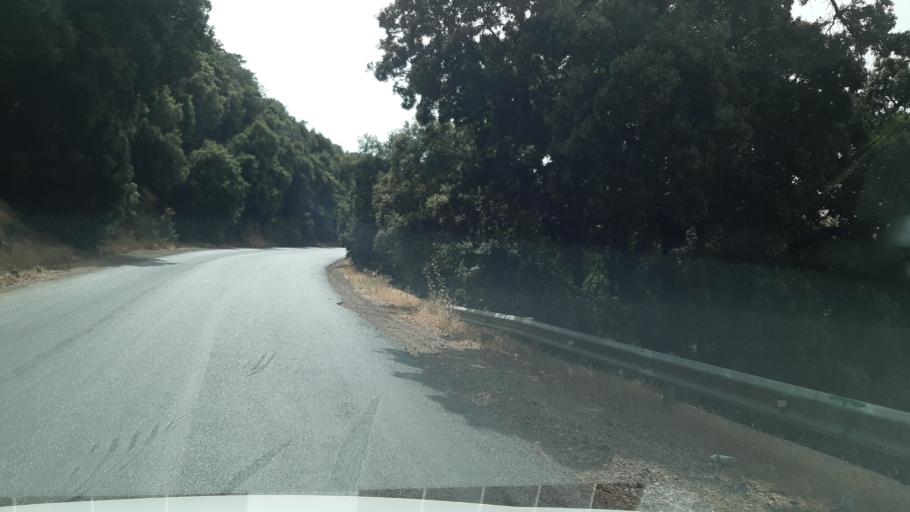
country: MA
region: Meknes-Tafilalet
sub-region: Ifrane
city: Azrou
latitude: 33.4279
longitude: -5.1995
